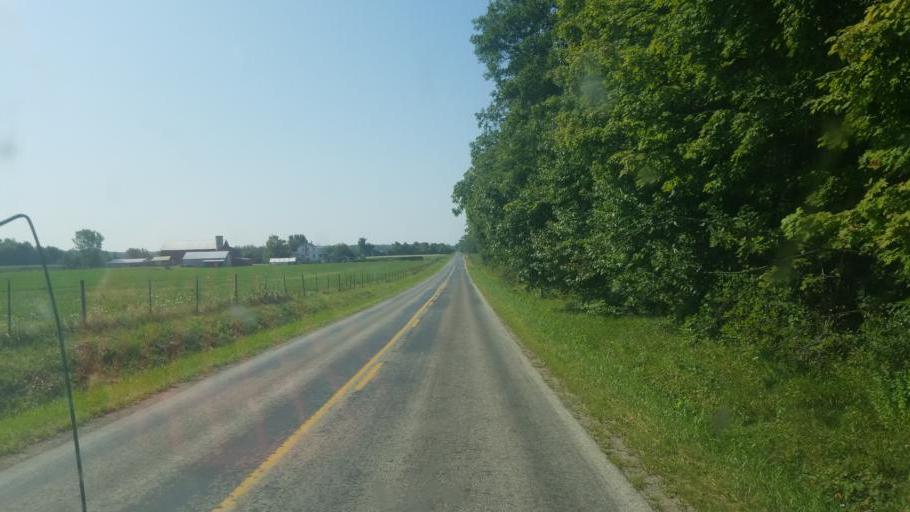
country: US
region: Ohio
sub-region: Wayne County
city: West Salem
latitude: 41.0369
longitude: -82.1821
